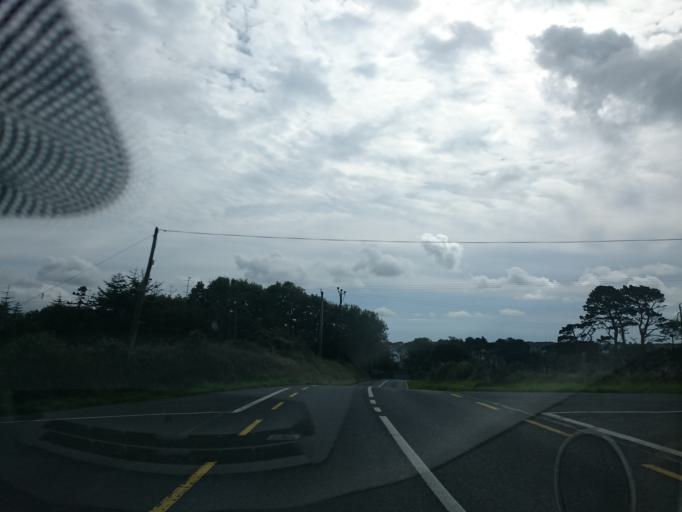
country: IE
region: Munster
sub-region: Waterford
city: Tra Mhor
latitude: 52.1760
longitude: -7.1619
